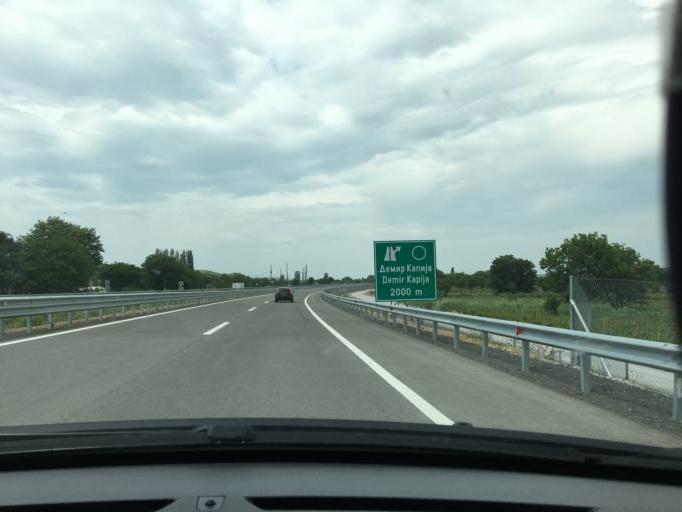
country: MK
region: Demir Kapija
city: Demir Kapija
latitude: 41.4102
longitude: 22.2494
